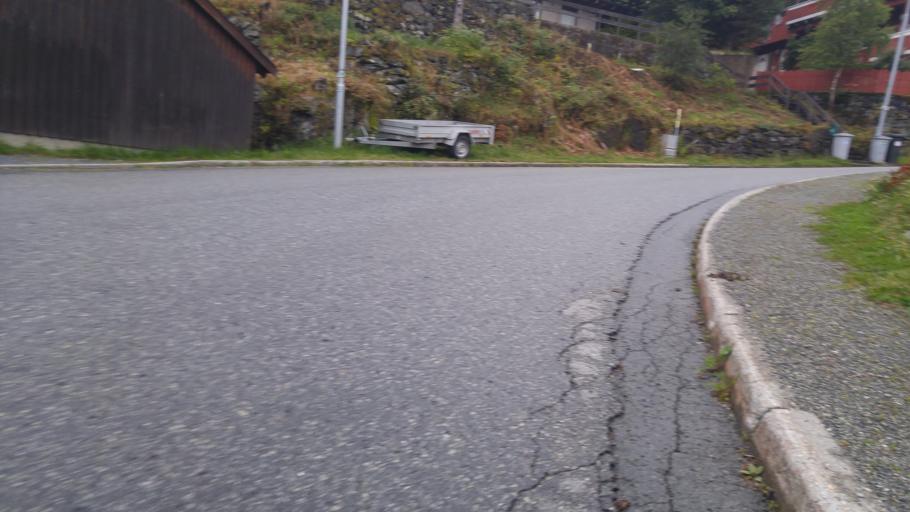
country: NO
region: Sor-Trondelag
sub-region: Trondheim
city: Trondheim
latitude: 63.4513
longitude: 10.3027
